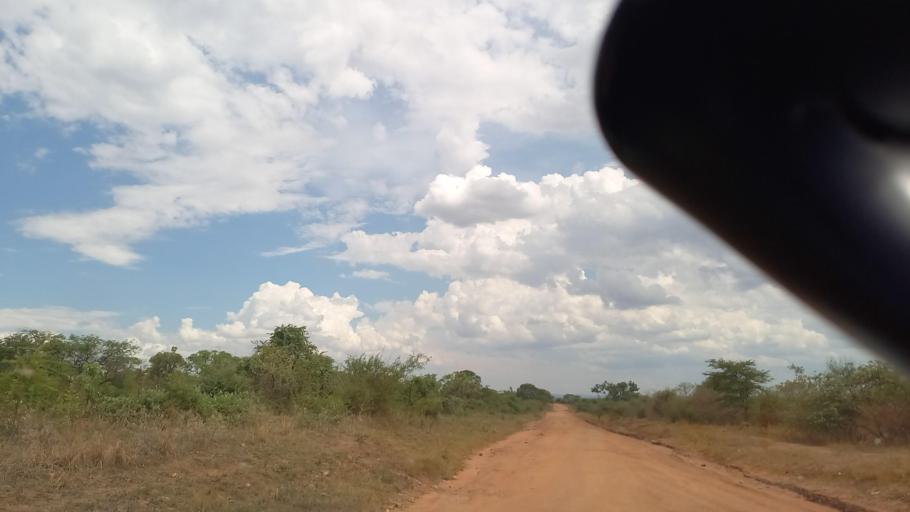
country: ZM
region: Southern
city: Nakambala
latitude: -16.0408
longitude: 27.9734
